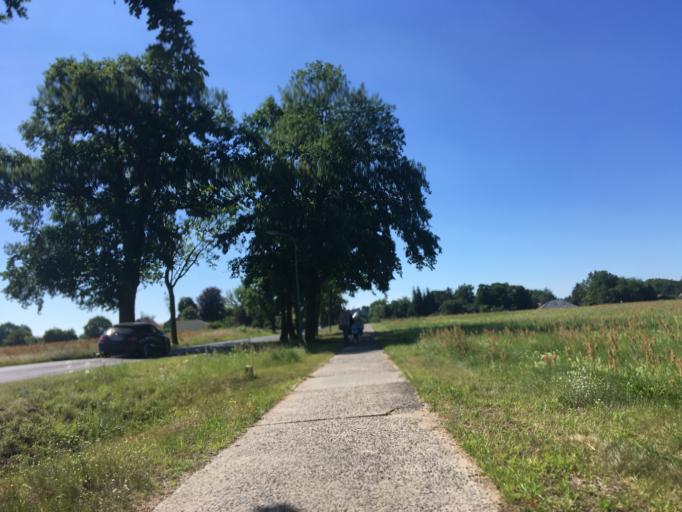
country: DE
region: Brandenburg
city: Petershagen
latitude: 52.5180
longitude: 13.7700
